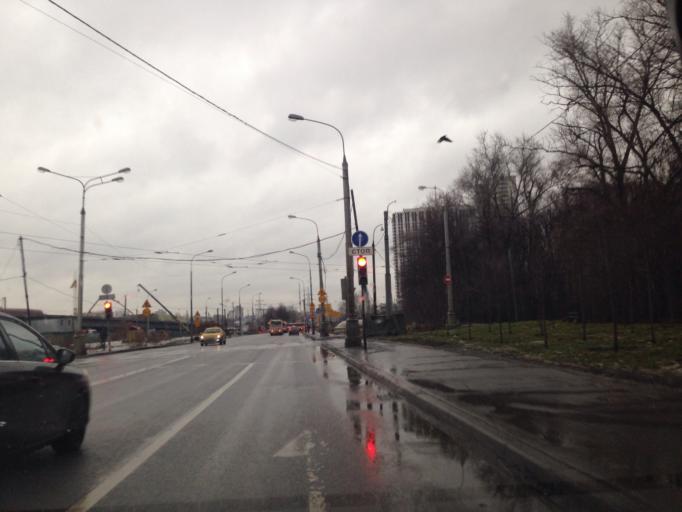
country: RU
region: Moskovskaya
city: Bogorodskoye
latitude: 55.7851
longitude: 37.7460
